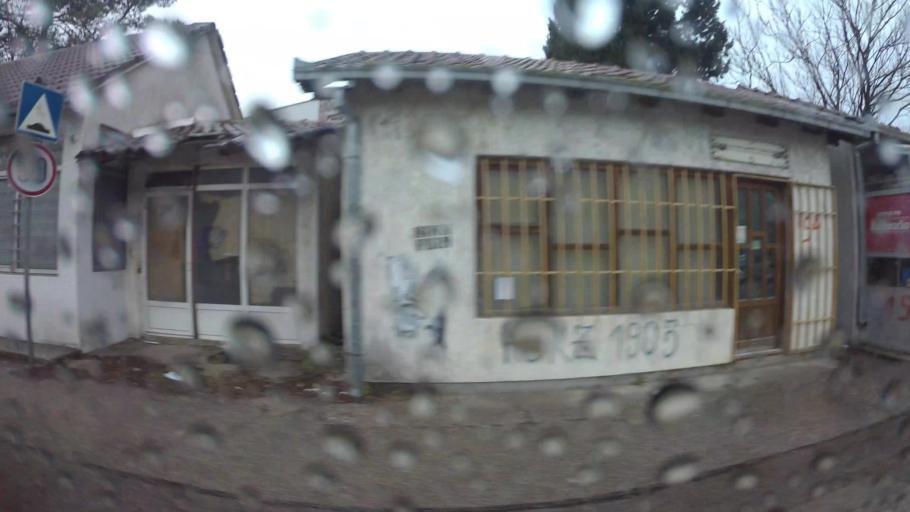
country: BA
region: Federation of Bosnia and Herzegovina
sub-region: Hercegovacko-Bosanski Kanton
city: Mostar
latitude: 43.3529
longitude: 17.8007
